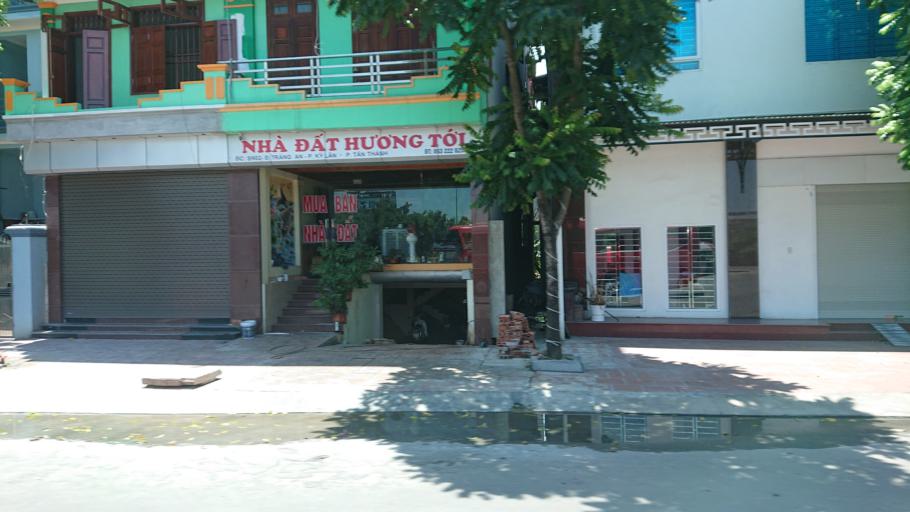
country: VN
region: Ninh Binh
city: Thanh Pho Ninh Binh
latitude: 20.2644
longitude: 105.9657
